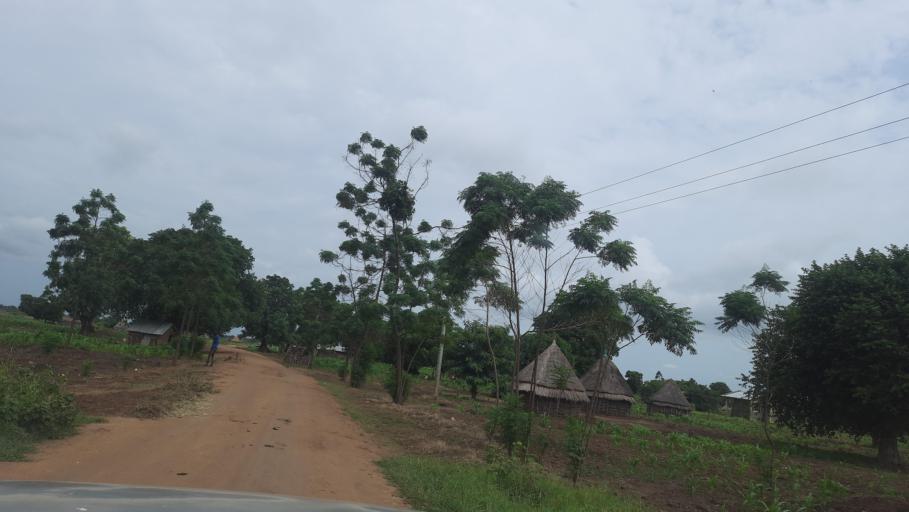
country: ET
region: Gambela
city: Gambela
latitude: 8.3279
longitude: 33.7094
